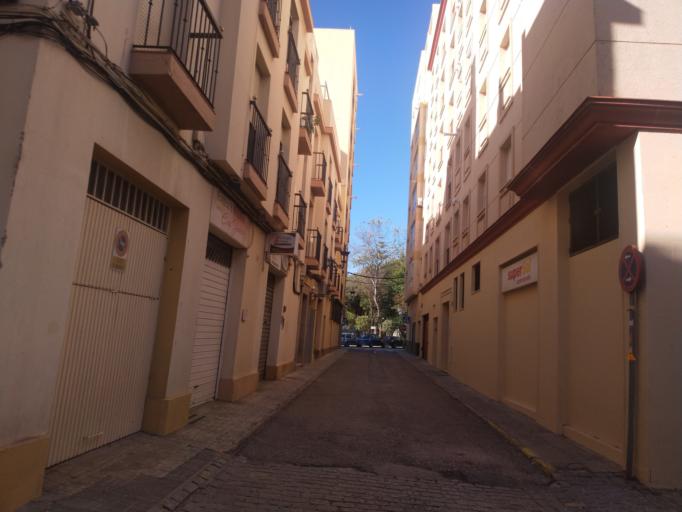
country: ES
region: Andalusia
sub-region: Provincia de Cadiz
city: San Fernando
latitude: 36.4657
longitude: -6.1999
